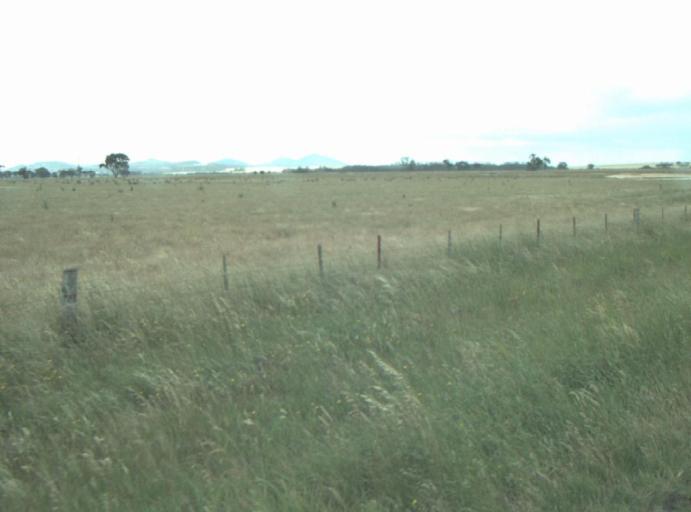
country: AU
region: Victoria
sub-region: Greater Geelong
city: Lara
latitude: -37.8531
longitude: 144.3532
